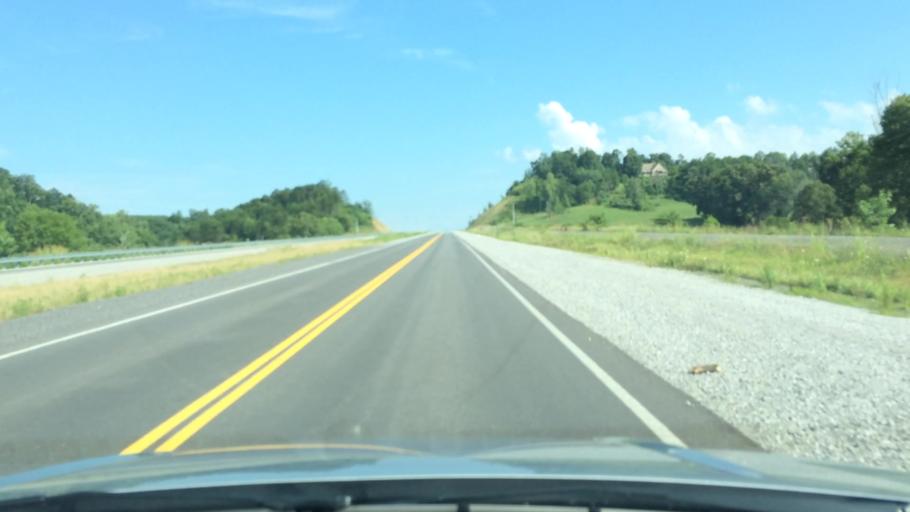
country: US
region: Tennessee
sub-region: Jefferson County
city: White Pine
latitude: 36.1311
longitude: -83.3360
